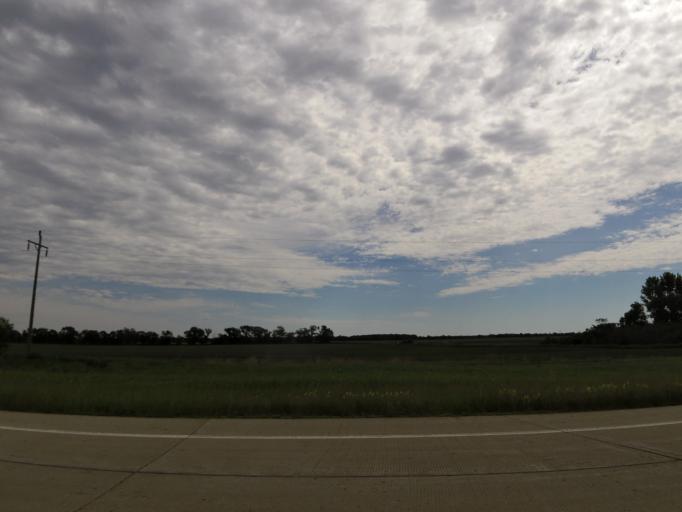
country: US
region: North Dakota
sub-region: Grand Forks County
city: Grand Forks
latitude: 48.1387
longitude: -97.1906
